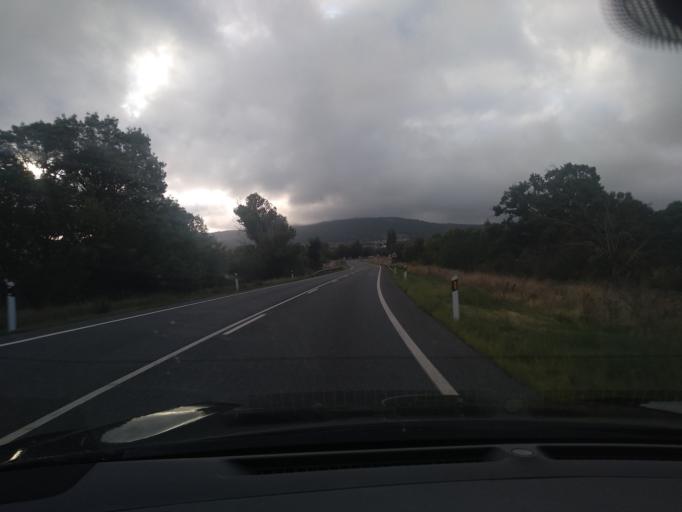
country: ES
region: Castille and Leon
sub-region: Provincia de Segovia
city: Otero de Herreros
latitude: 40.7532
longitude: -4.2036
